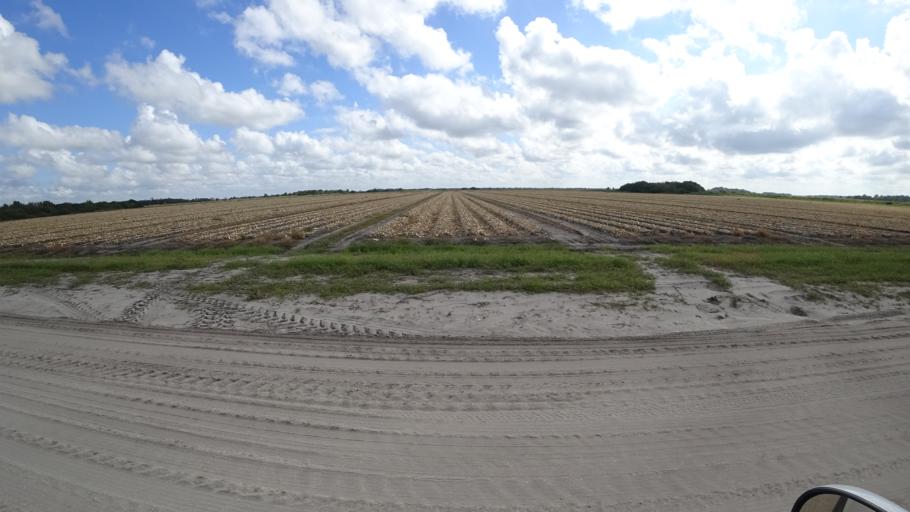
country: US
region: Florida
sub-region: Sarasota County
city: Lake Sarasota
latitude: 27.4381
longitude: -82.1825
